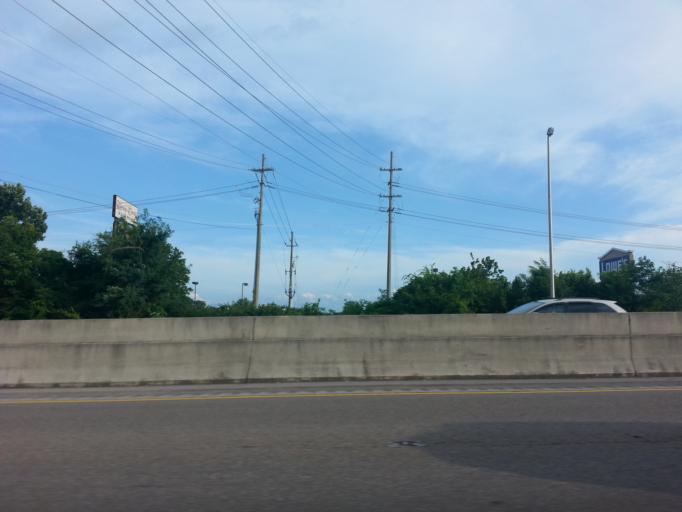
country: US
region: Tennessee
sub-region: Knox County
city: Farragut
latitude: 35.9202
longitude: -84.0816
